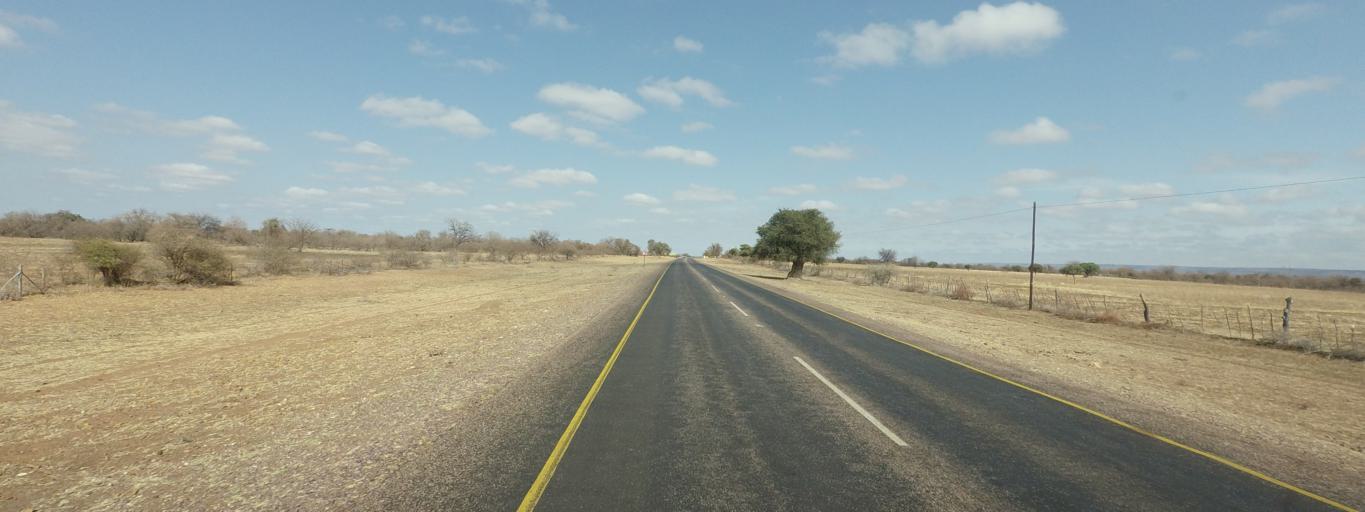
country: BW
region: Central
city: Ramokgonami
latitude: -22.8021
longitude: 27.4990
